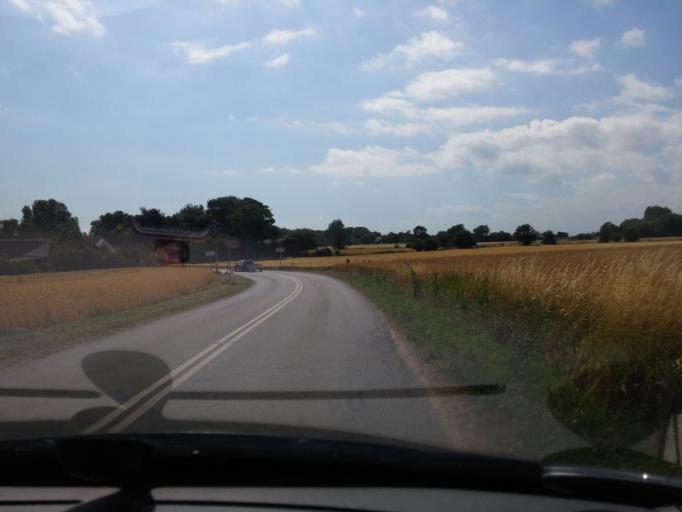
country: DK
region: South Denmark
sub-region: Langeland Kommune
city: Rudkobing
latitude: 54.8207
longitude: 10.6816
